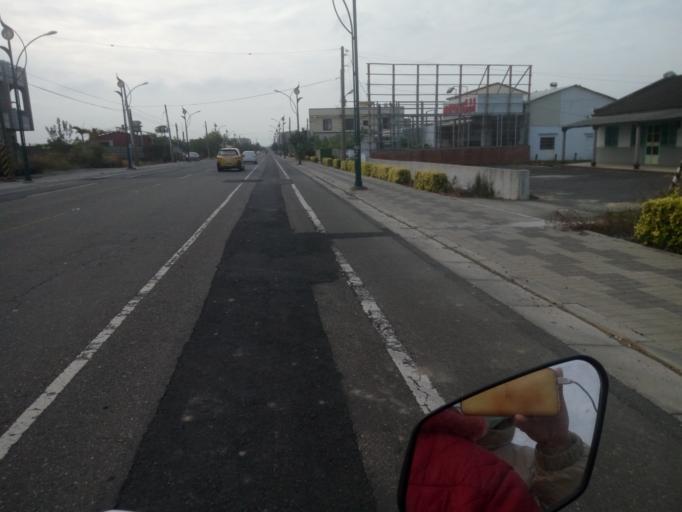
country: TW
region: Taiwan
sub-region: Chiayi
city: Taibao
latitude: 23.4909
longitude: 120.3505
